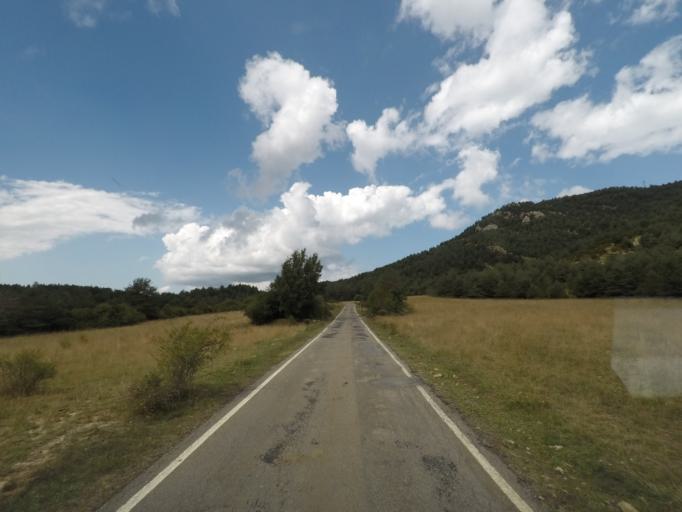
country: ES
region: Aragon
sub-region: Provincia de Huesca
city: Fiscal
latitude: 42.4039
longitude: -0.0601
